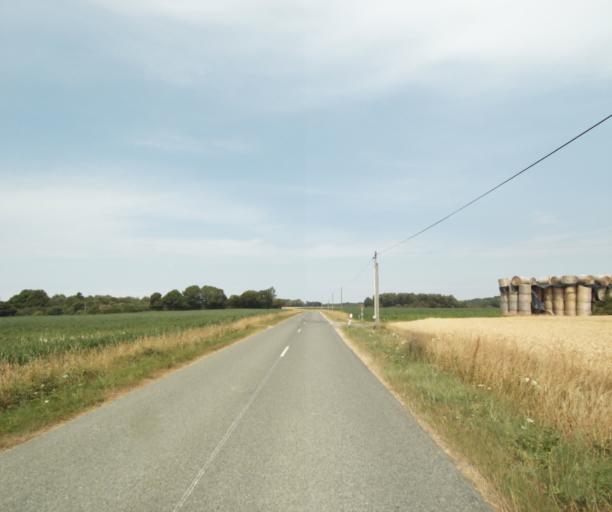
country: FR
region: Centre
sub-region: Departement d'Eure-et-Loir
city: La Bazoche-Gouet
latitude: 48.1804
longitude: 0.9458
